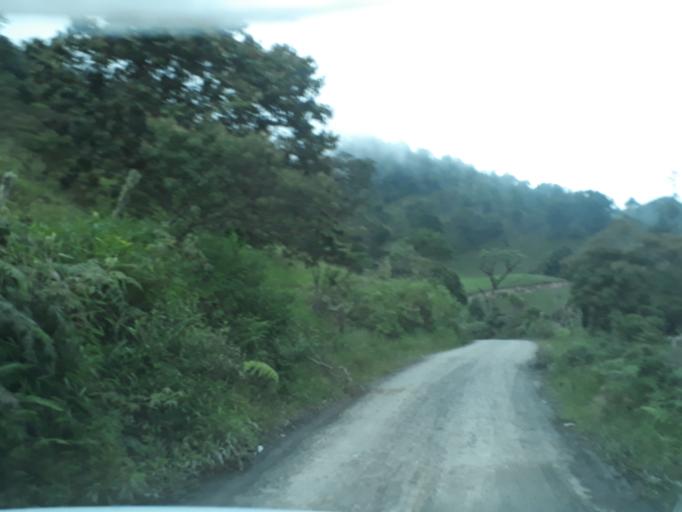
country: CO
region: Boyaca
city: Muzo
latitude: 5.3698
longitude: -74.0713
